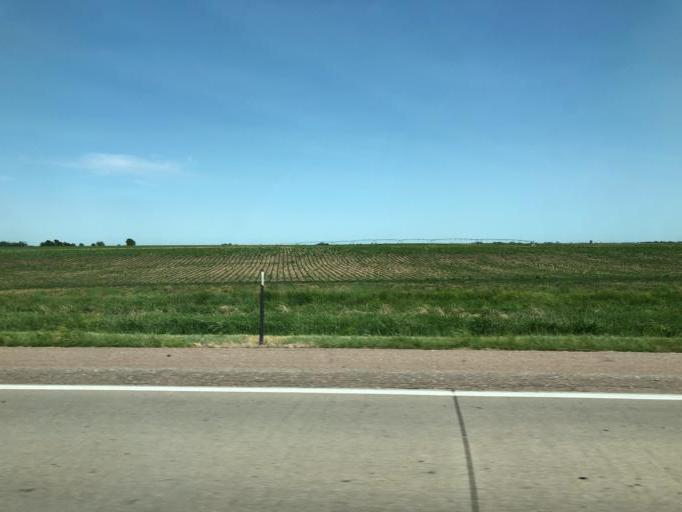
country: US
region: Nebraska
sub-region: Fillmore County
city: Geneva
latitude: 40.6587
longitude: -97.5957
